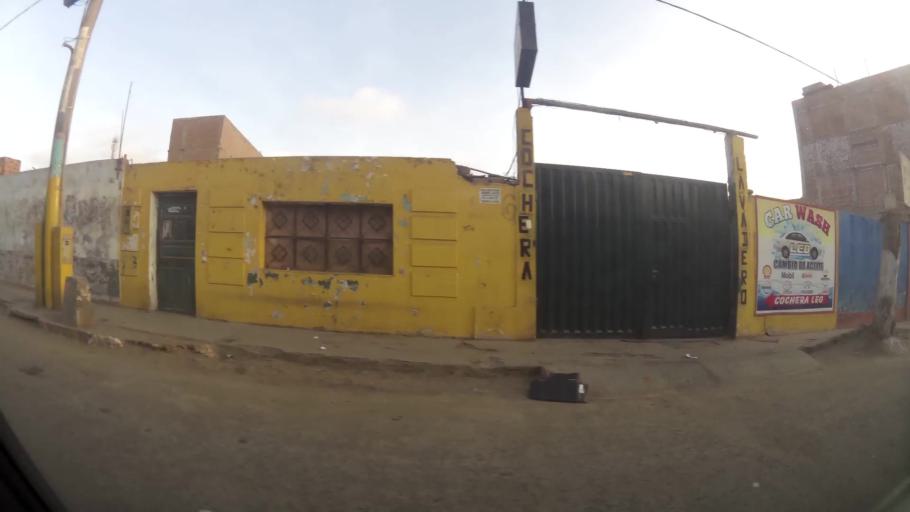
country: PE
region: Lima
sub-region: Huaura
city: Huacho
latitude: -11.1082
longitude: -77.5997
